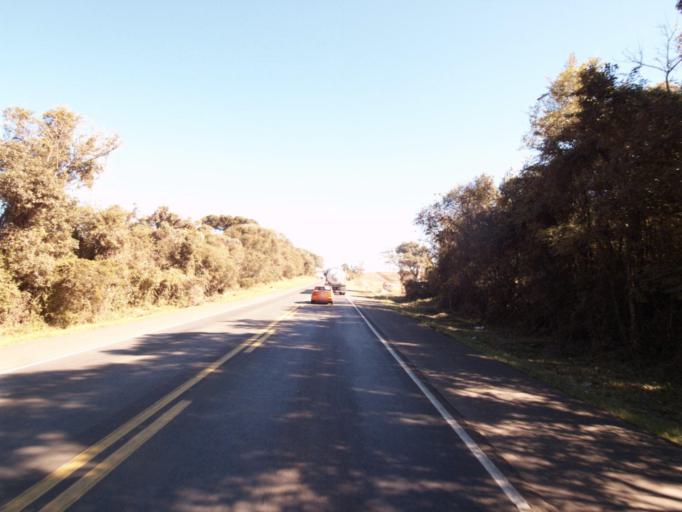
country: BR
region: Santa Catarina
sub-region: Xanxere
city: Xanxere
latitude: -26.8724
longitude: -52.2779
